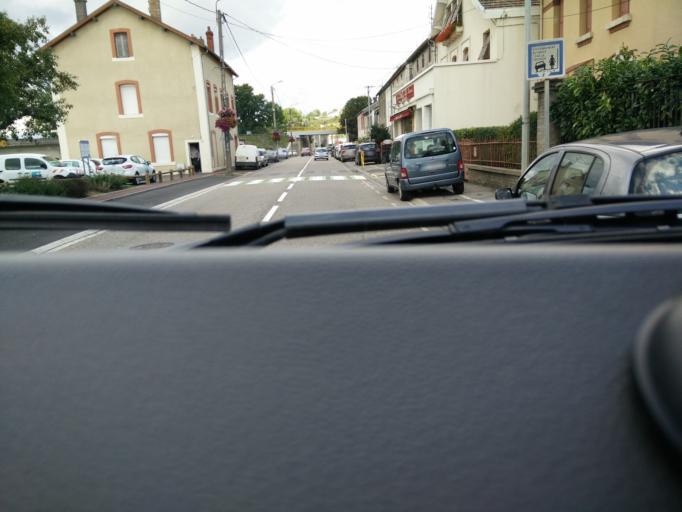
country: FR
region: Lorraine
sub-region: Departement de la Meuse
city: Verdun
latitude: 49.1720
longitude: 5.3834
